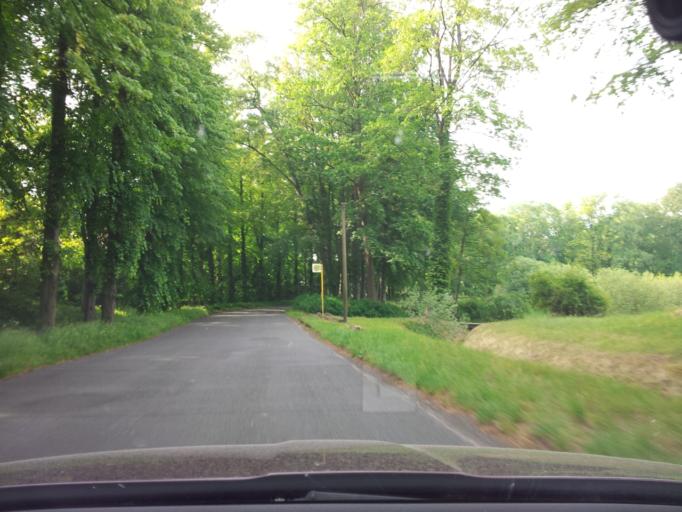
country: DE
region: Brandenburg
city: Werder
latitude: 52.3429
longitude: 12.9403
